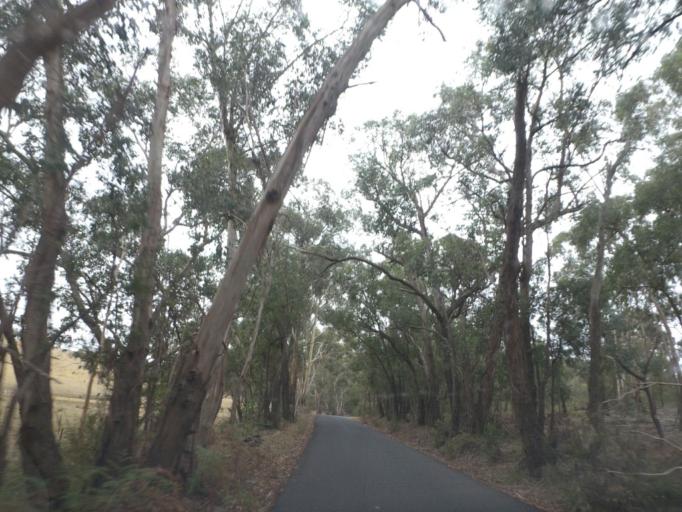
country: AU
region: Victoria
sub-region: Yarra Ranges
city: Yarra Glen
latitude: -37.6324
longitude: 145.3367
